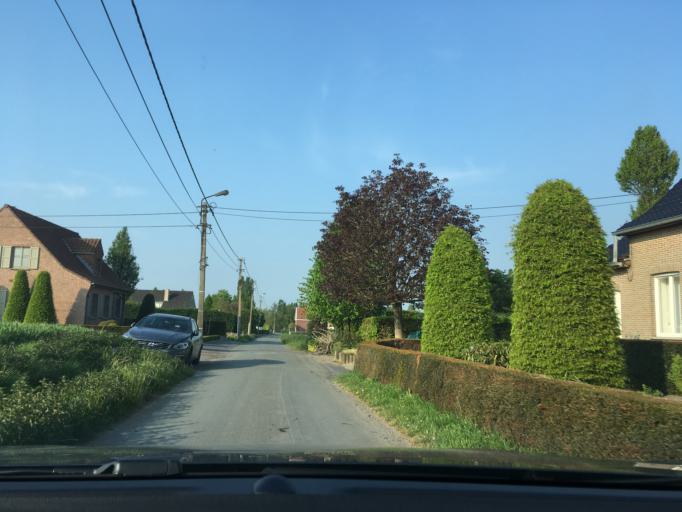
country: BE
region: Flanders
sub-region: Provincie West-Vlaanderen
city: Lichtervelde
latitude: 51.0102
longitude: 3.1429
